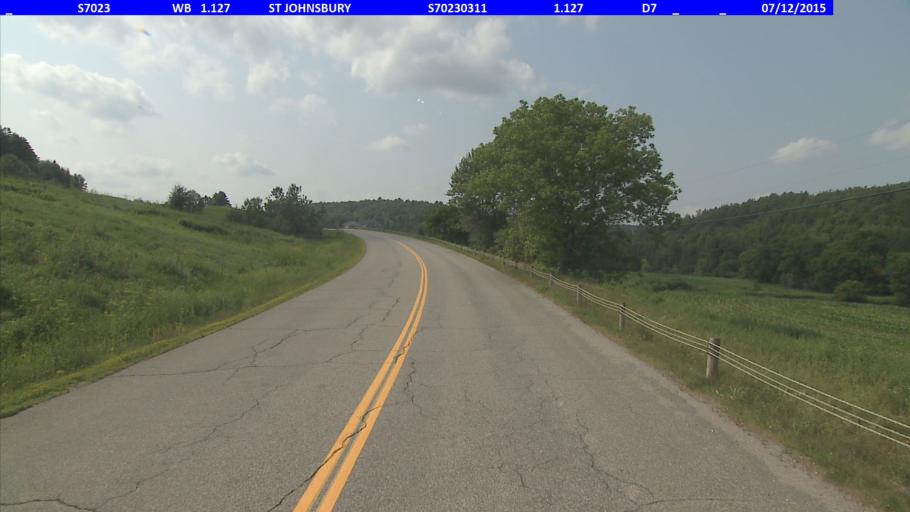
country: US
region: Vermont
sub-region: Caledonia County
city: St Johnsbury
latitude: 44.4411
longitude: -72.0426
